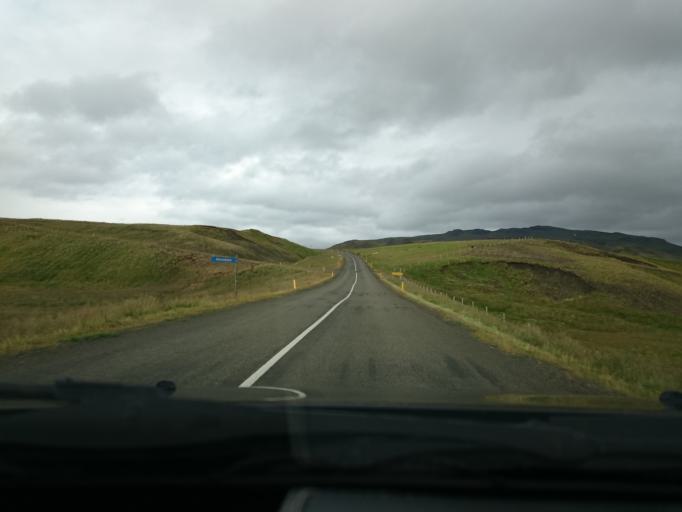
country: IS
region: West
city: Stykkisholmur
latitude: 65.4709
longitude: -21.9167
